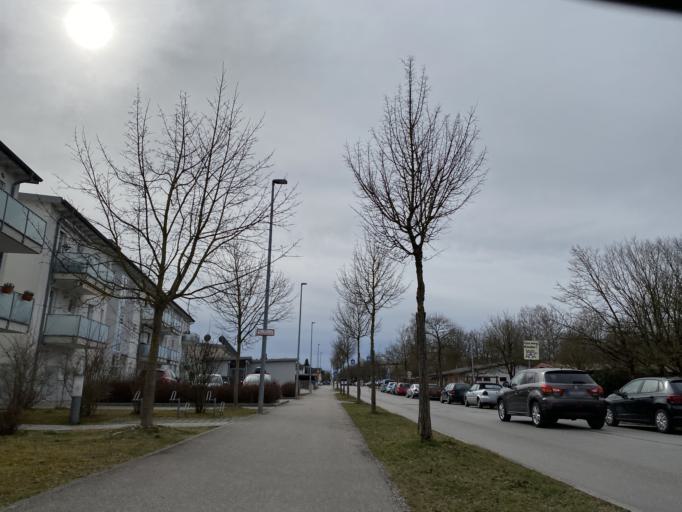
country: DE
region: Bavaria
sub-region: Upper Bavaria
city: Fuerstenfeldbruck
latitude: 48.1687
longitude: 11.2266
